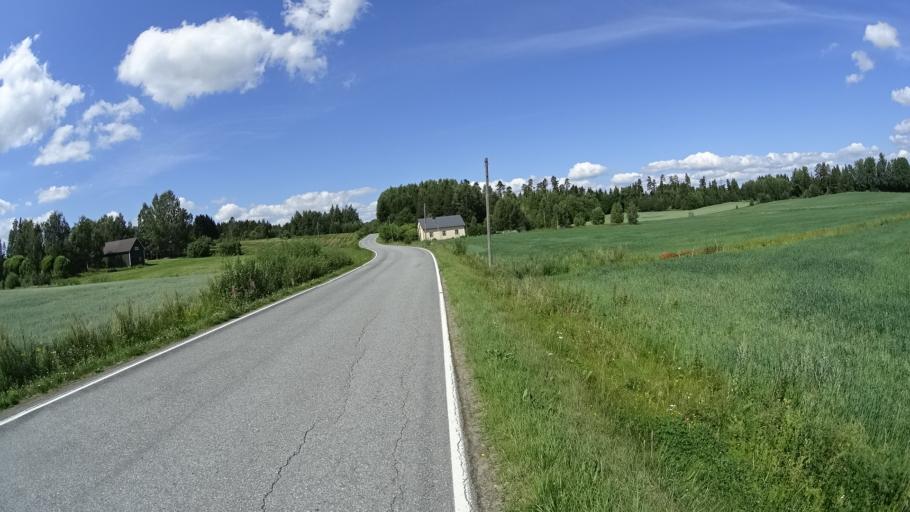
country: FI
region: Haeme
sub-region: Forssa
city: Tammela
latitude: 60.7625
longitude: 23.8810
